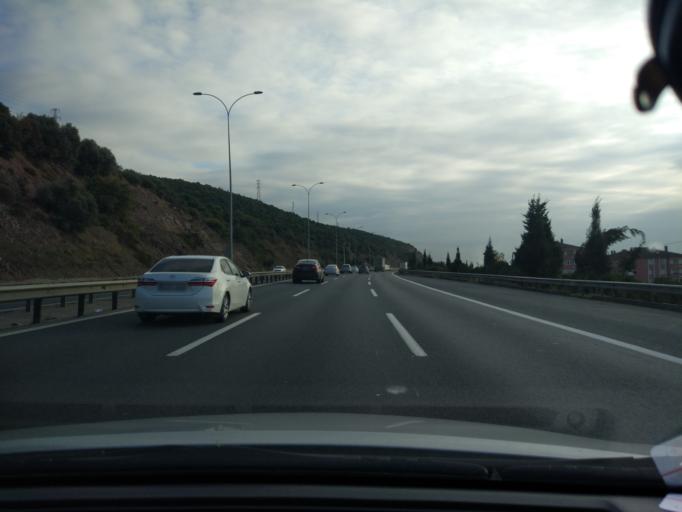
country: TR
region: Kocaeli
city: Hereke
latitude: 40.7799
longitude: 29.6651
